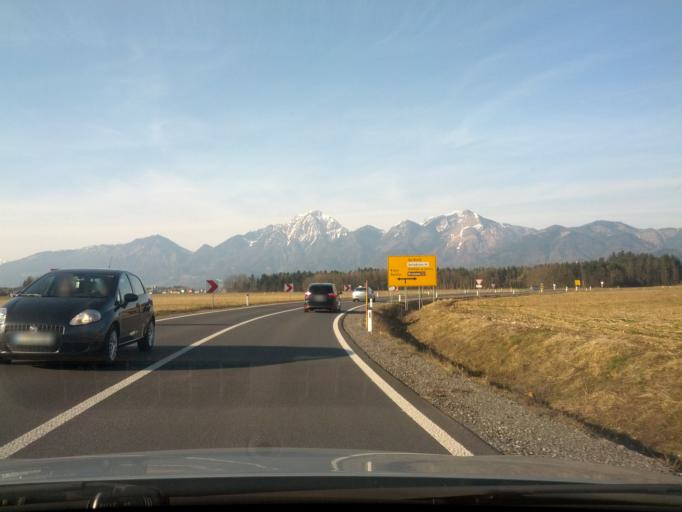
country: SI
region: Sencur
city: Sencur
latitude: 46.2341
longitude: 14.4318
